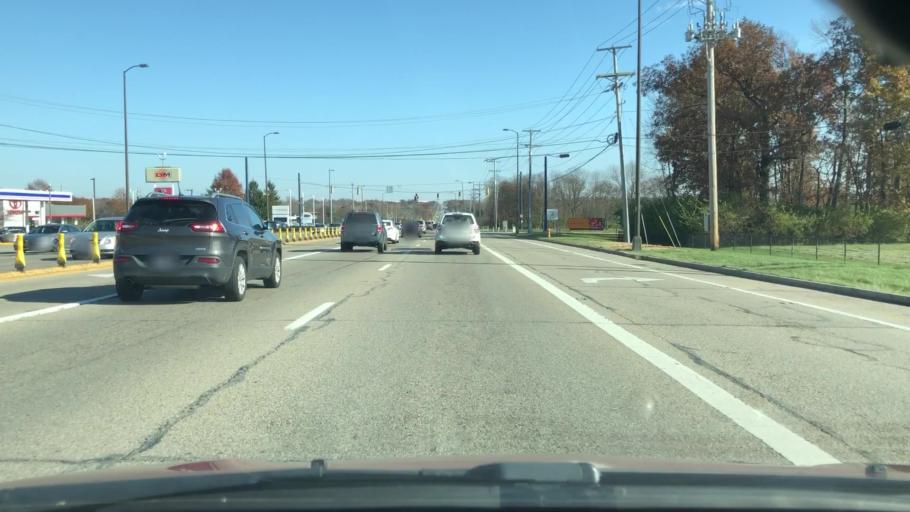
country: US
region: Ohio
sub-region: Franklin County
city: Huber Ridge
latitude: 40.0569
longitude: -82.8992
